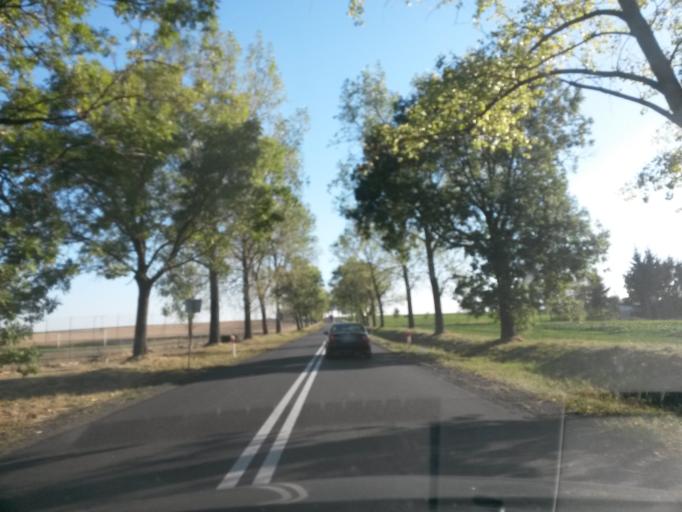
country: PL
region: Lower Silesian Voivodeship
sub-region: Powiat sredzki
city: Udanin
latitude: 51.0421
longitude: 16.3990
